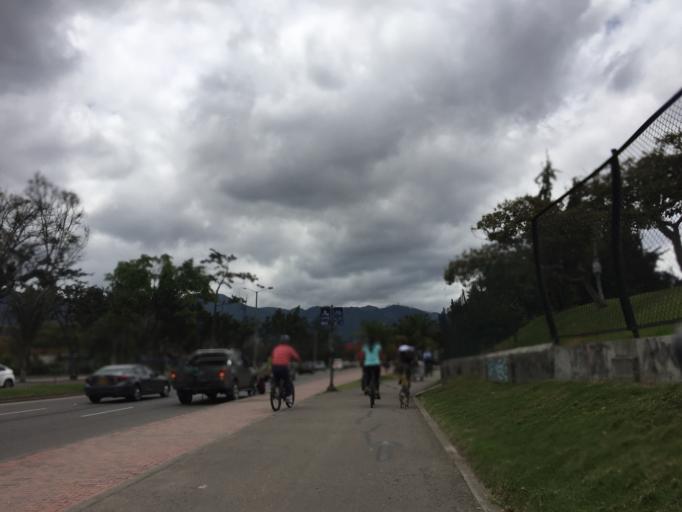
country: CO
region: Bogota D.C.
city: Bogota
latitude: 4.6618
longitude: -74.0904
